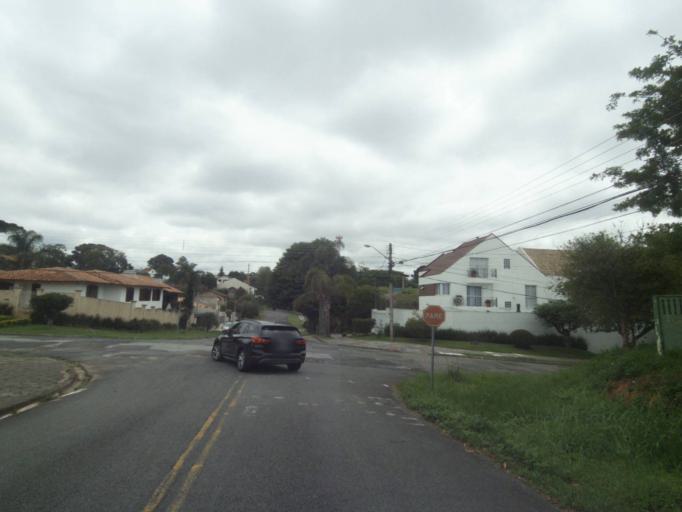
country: BR
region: Parana
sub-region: Curitiba
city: Curitiba
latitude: -25.3907
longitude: -49.2741
